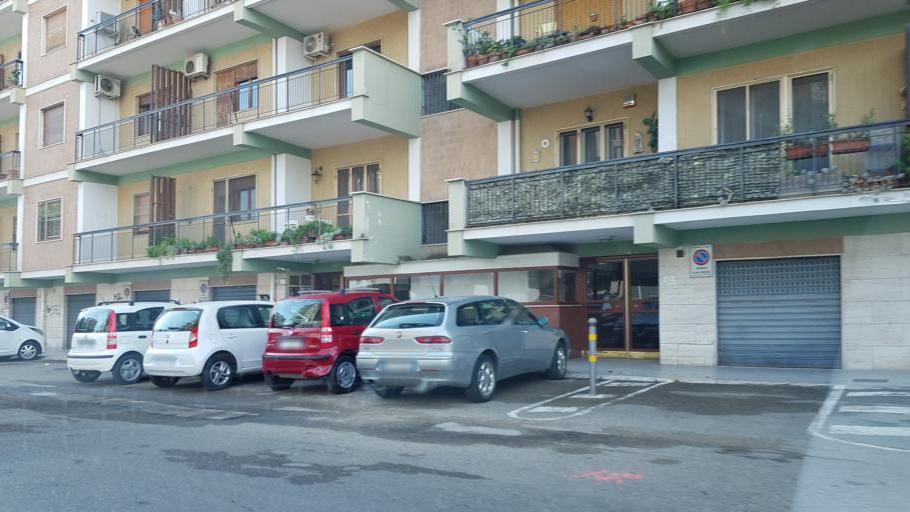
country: IT
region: Apulia
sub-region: Provincia di Foggia
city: Foggia
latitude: 41.4553
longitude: 15.5619
